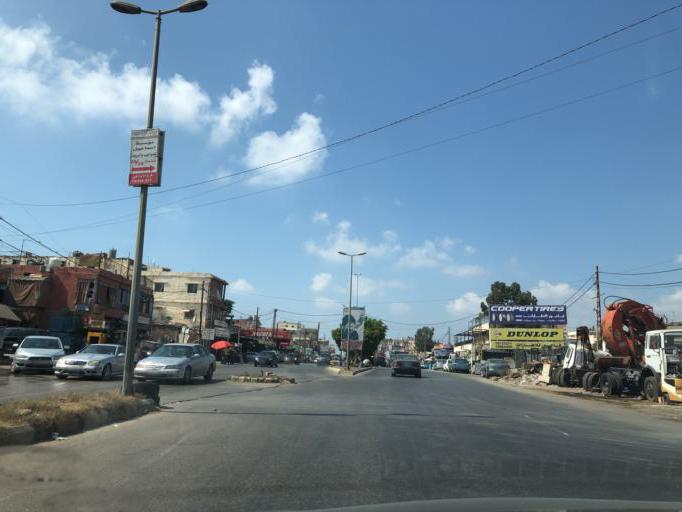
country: LB
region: Beyrouth
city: Beirut
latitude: 33.8307
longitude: 35.4843
